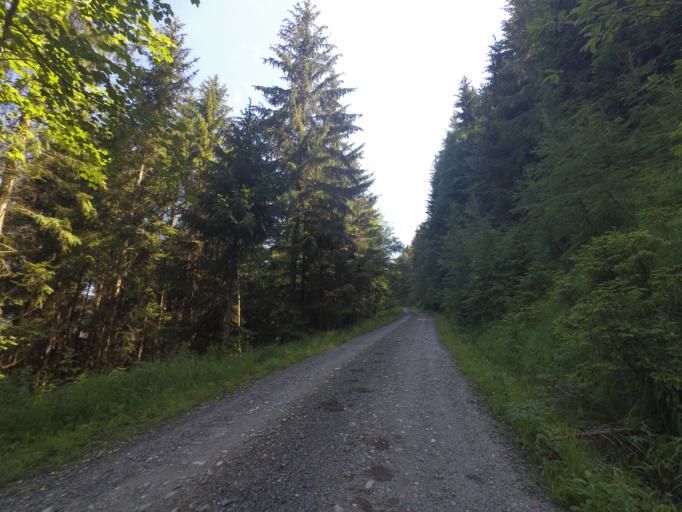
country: AT
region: Salzburg
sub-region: Politischer Bezirk Sankt Johann im Pongau
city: Schwarzach im Pongau
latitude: 47.3045
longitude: 13.1419
